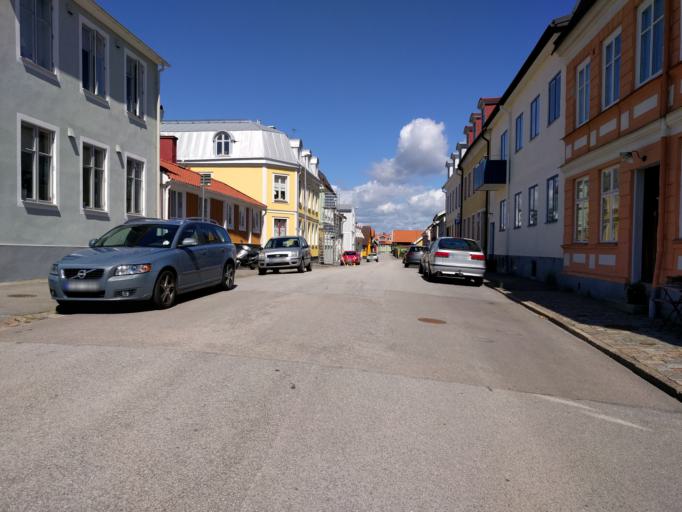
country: SE
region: Blekinge
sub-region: Karlskrona Kommun
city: Karlskrona
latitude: 56.1610
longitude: 15.5726
